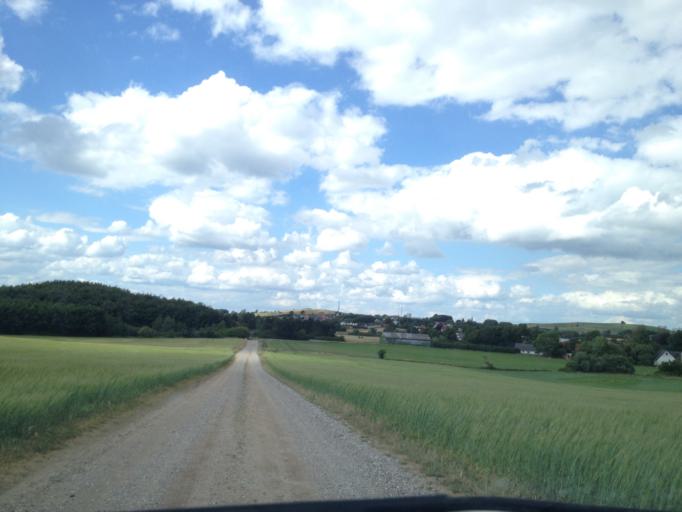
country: DK
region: Central Jutland
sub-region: Syddjurs Kommune
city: Ronde
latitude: 56.2025
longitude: 10.4844
